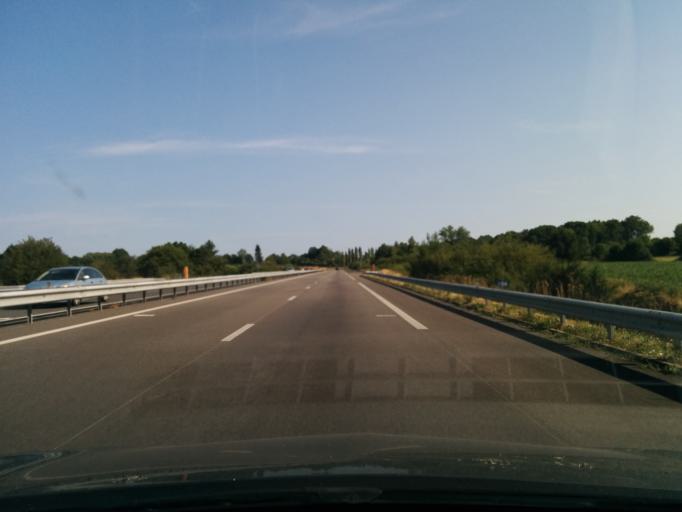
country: FR
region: Limousin
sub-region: Departement de la Haute-Vienne
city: Vicq-sur-Breuilh
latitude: 45.6521
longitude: 1.4040
